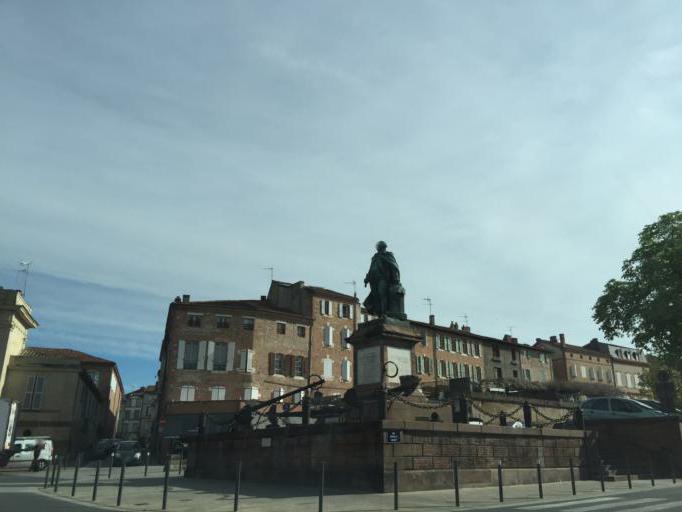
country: FR
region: Midi-Pyrenees
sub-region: Departement du Tarn
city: Albi
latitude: 43.9253
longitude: 2.1455
